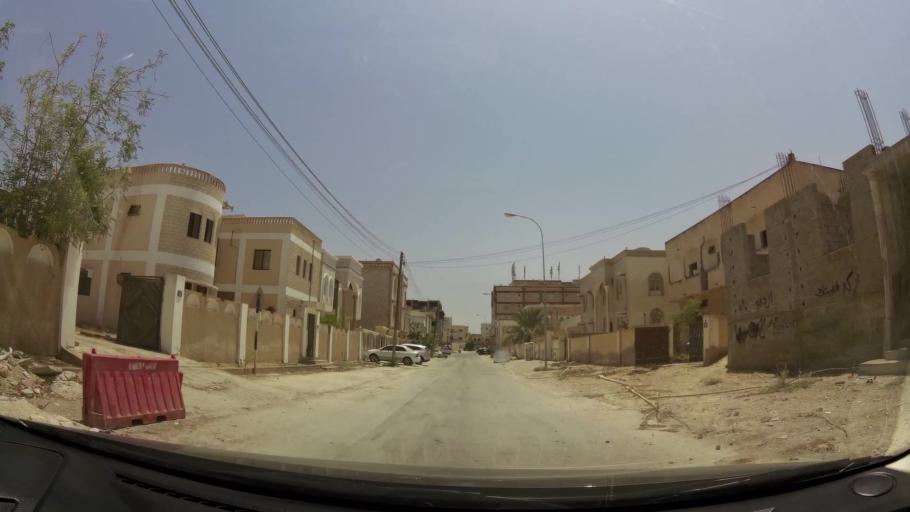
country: OM
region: Zufar
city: Salalah
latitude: 17.0223
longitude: 54.0821
